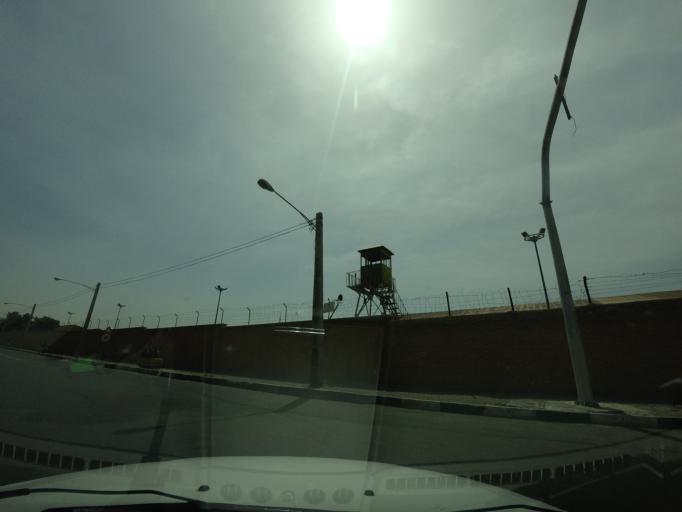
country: IR
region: Tehran
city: Shahr-e Qods
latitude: 35.7439
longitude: 51.2284
